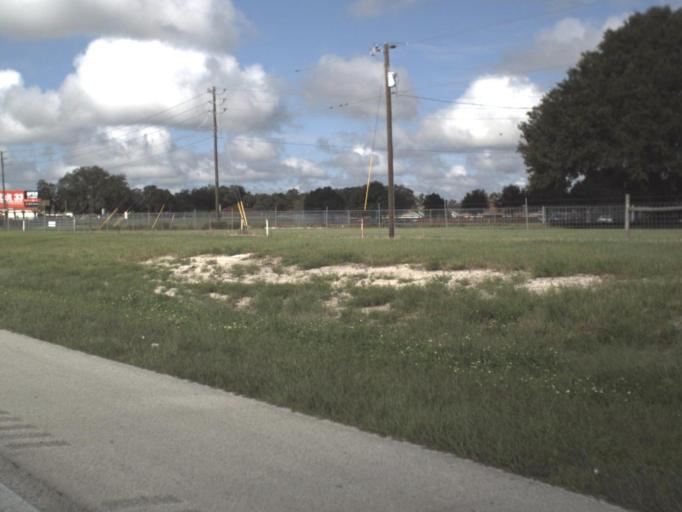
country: US
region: Florida
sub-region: Polk County
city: Gibsonia
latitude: 28.1294
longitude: -81.9210
